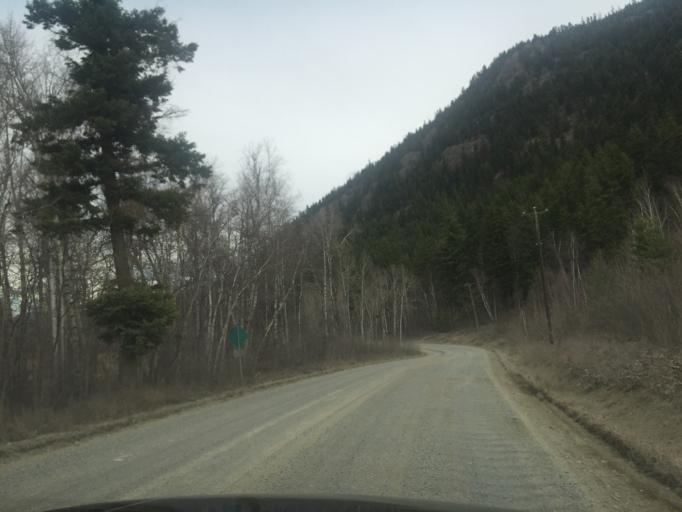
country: CA
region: British Columbia
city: Kamloops
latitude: 51.2761
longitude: -120.1531
